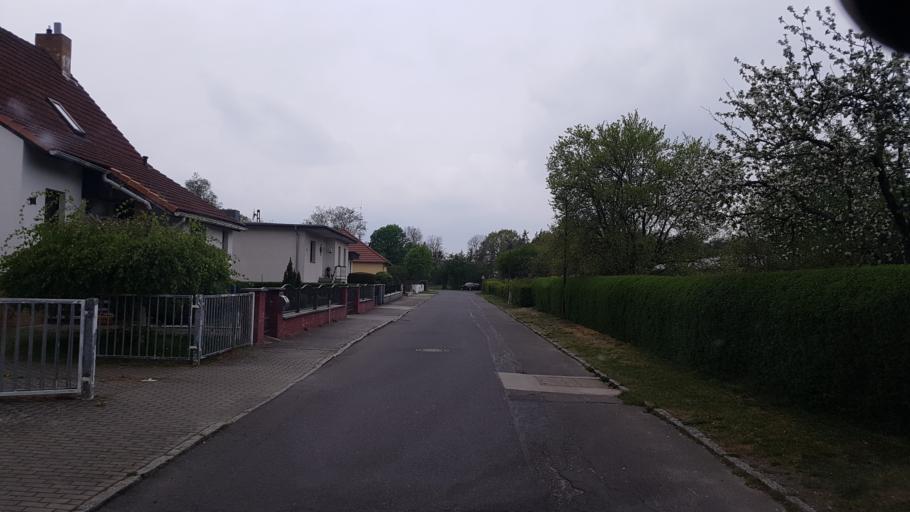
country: DE
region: Brandenburg
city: Grossraschen
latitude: 51.5844
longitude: 13.9658
